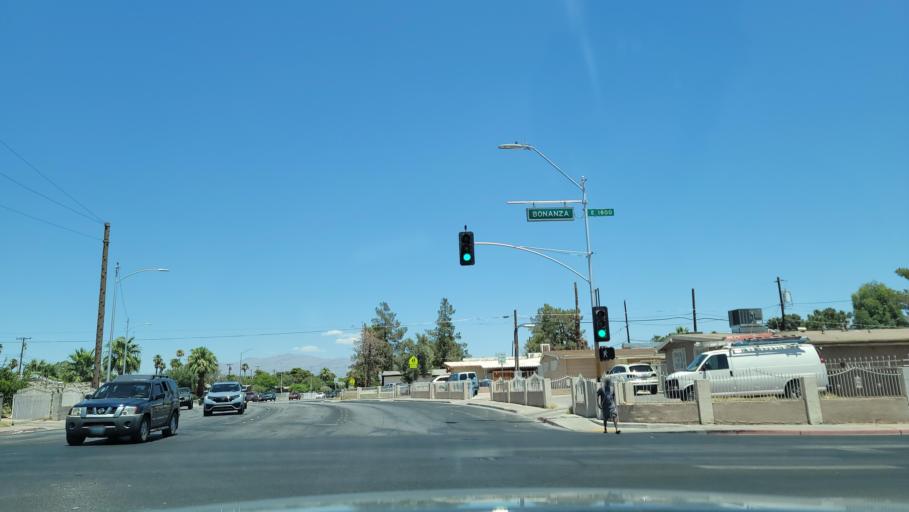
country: US
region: Nevada
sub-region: Clark County
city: Las Vegas
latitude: 36.1739
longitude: -115.1251
